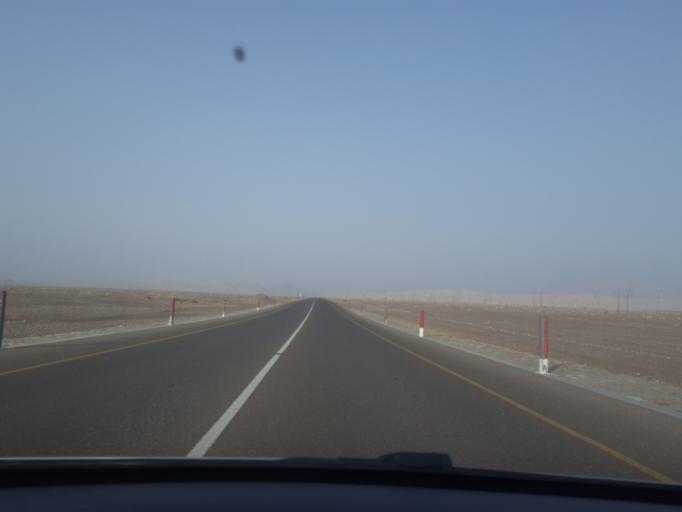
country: AE
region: Abu Dhabi
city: Al Ain
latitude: 24.0159
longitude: 55.9524
